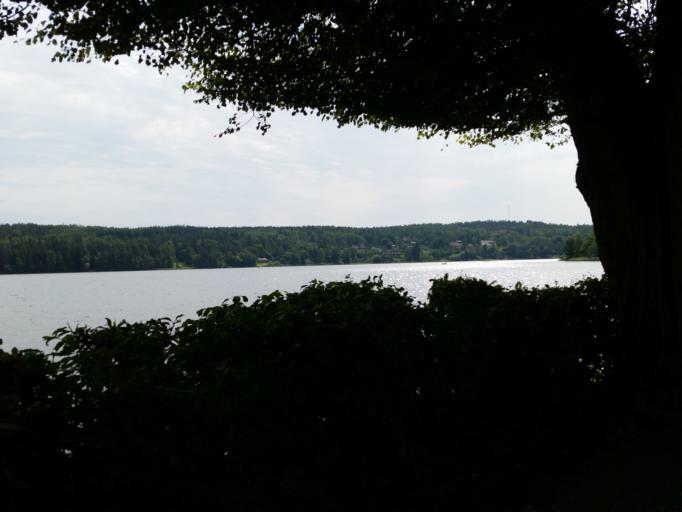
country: SE
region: Soedermanland
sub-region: Strangnas Kommun
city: Mariefred
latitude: 59.2550
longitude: 17.2201
